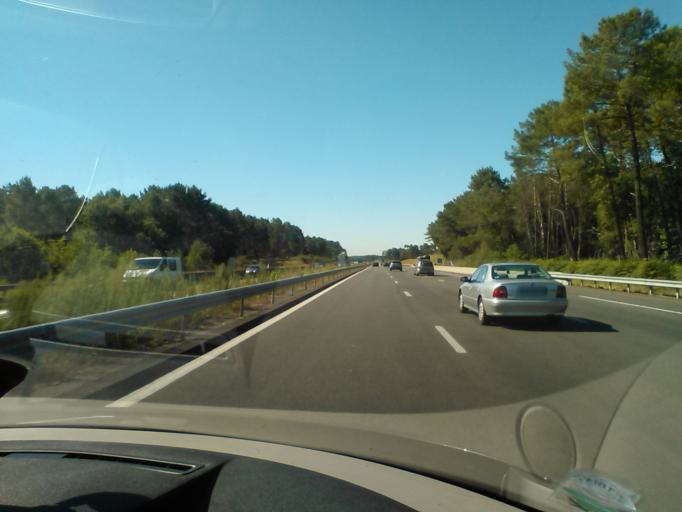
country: FR
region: Aquitaine
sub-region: Departement de la Gironde
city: Salles
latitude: 44.5445
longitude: -0.8339
